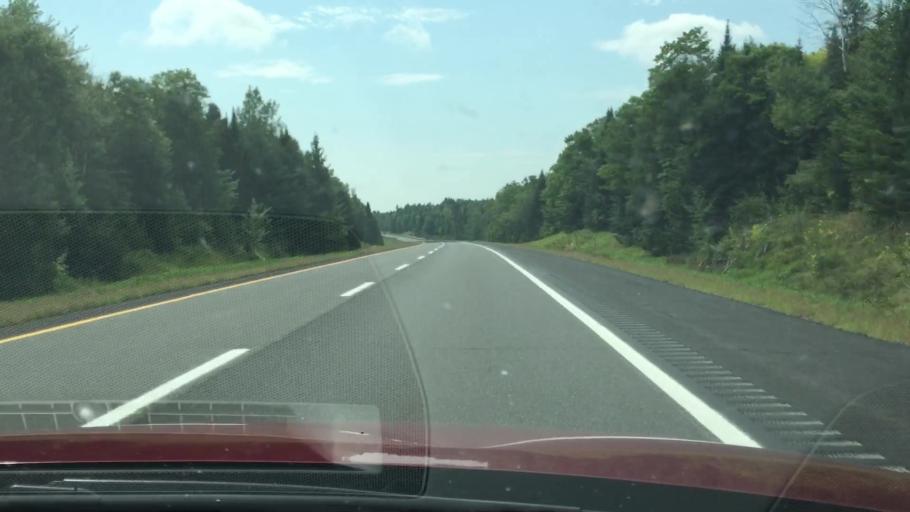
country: US
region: Maine
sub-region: Penobscot County
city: Patten
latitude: 46.0889
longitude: -68.2050
